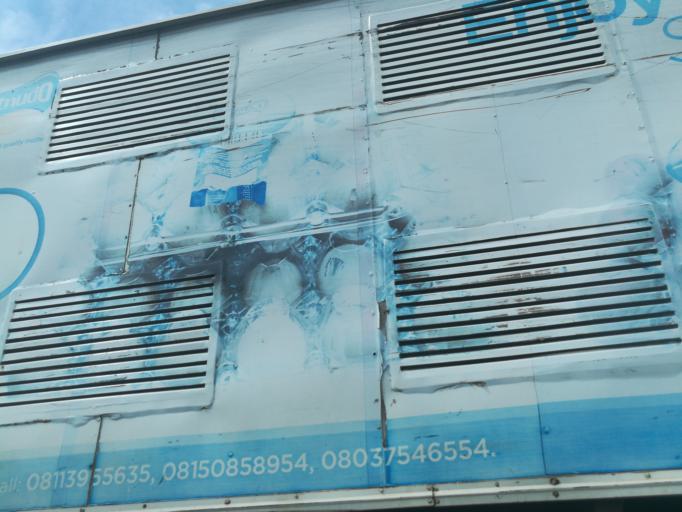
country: NG
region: Lagos
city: Agege
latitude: 6.6263
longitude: 3.3248
